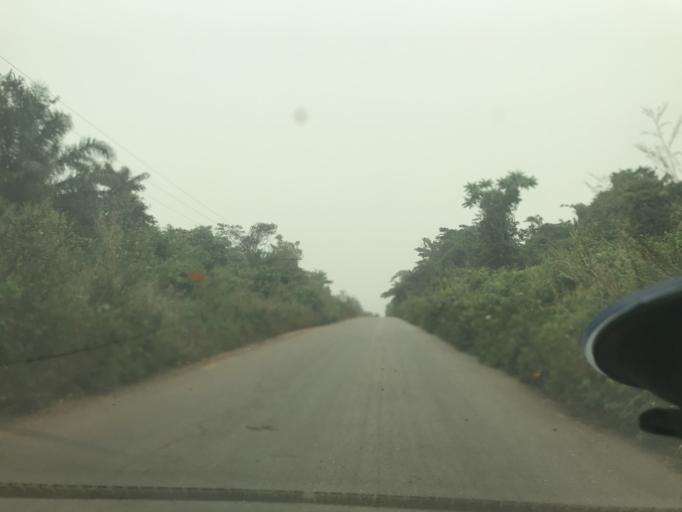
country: NG
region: Ogun
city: Owode
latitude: 6.8871
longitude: 3.5235
